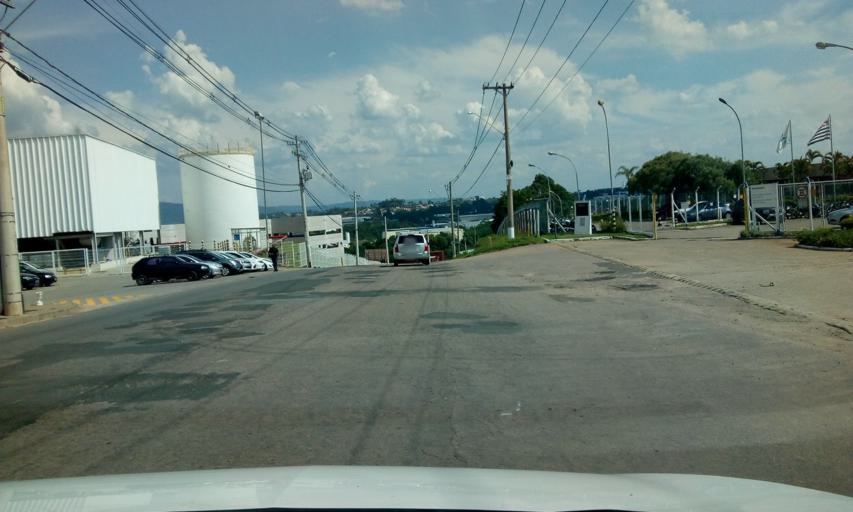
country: BR
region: Sao Paulo
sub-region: Itupeva
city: Itupeva
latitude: -23.1435
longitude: -47.0209
